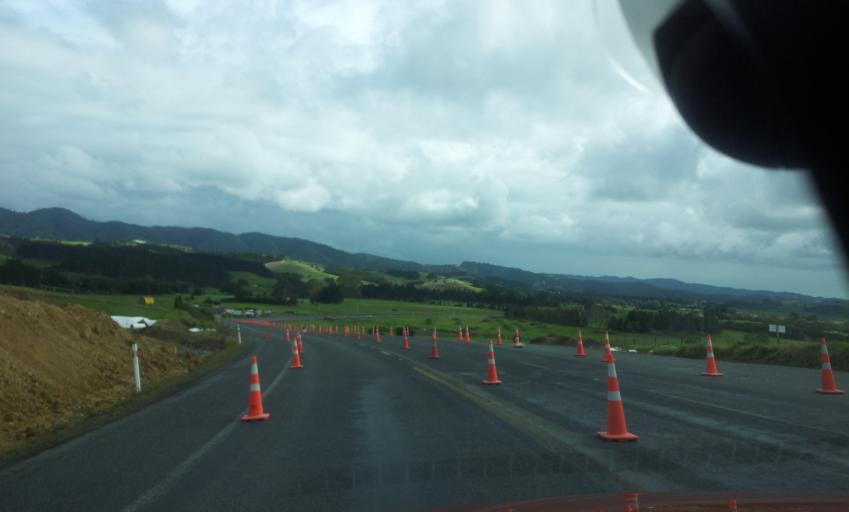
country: NZ
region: Northland
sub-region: Whangarei
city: Ruakaka
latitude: -36.0383
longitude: 174.4182
